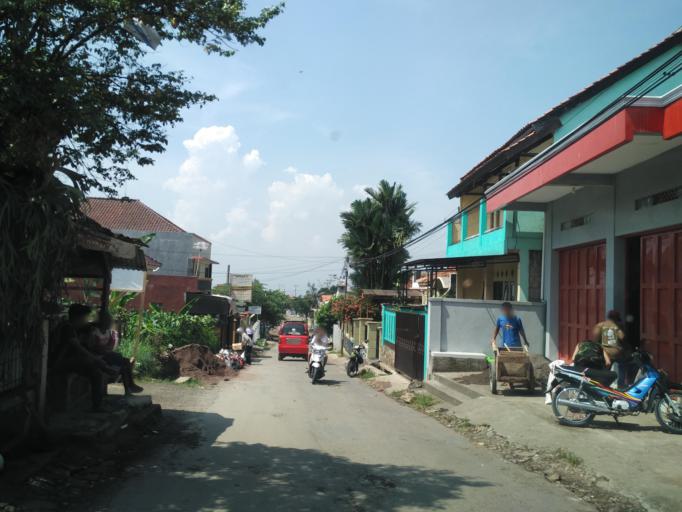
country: ID
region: West Java
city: Ciranjang-hilir
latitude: -6.8359
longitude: 107.1234
